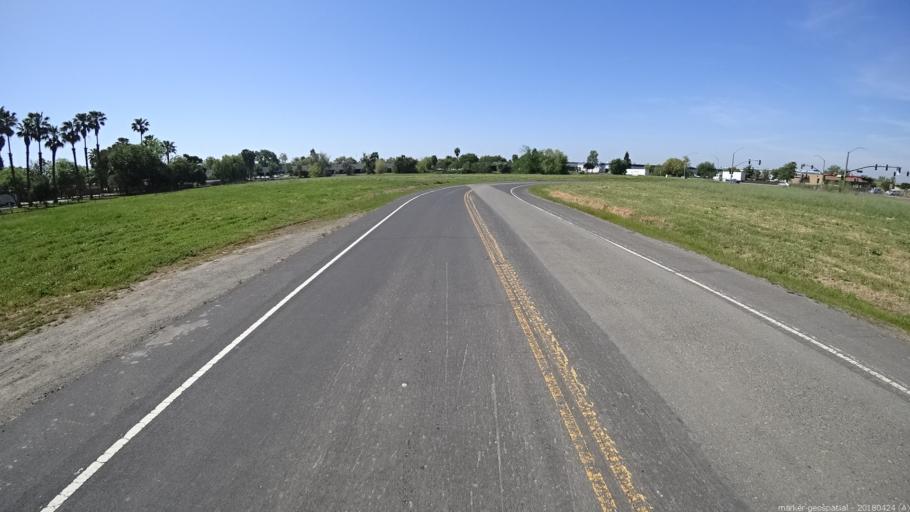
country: US
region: California
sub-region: Yolo County
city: West Sacramento
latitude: 38.5727
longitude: -121.5770
